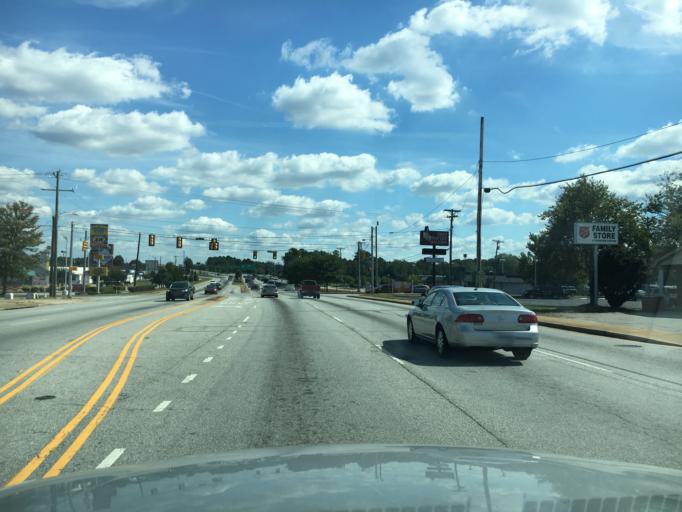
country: US
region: South Carolina
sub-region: Greenville County
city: Mauldin
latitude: 34.7774
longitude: -82.3090
